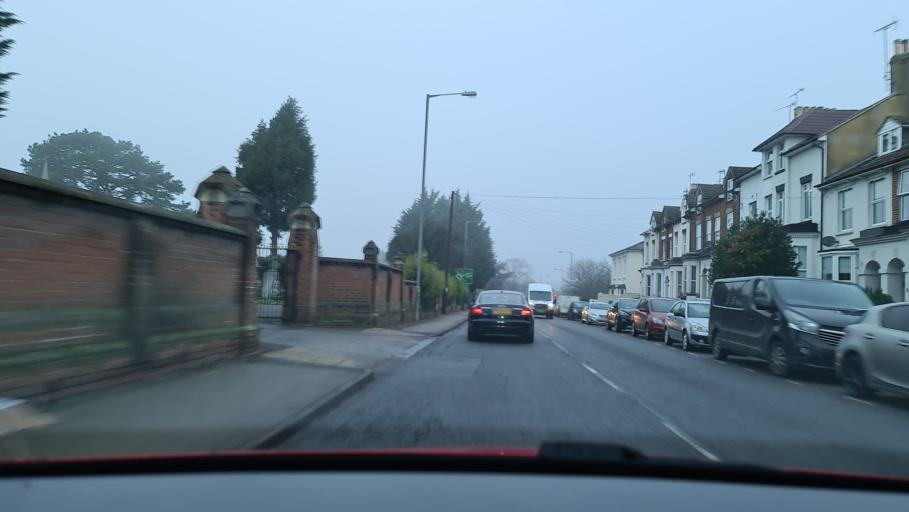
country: GB
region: England
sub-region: Buckinghamshire
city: Aylesbury
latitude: 51.8151
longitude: -0.7975
